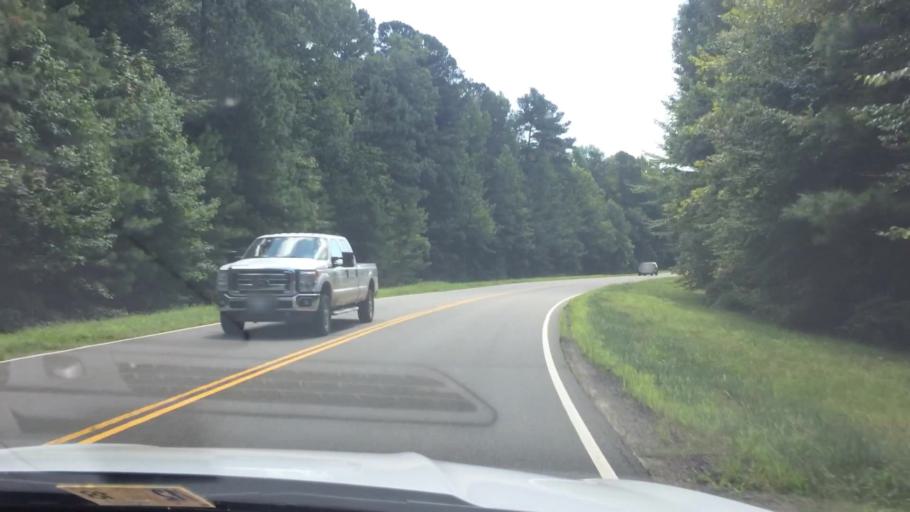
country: US
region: Virginia
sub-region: James City County
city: Williamsburg
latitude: 37.2953
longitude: -76.7350
